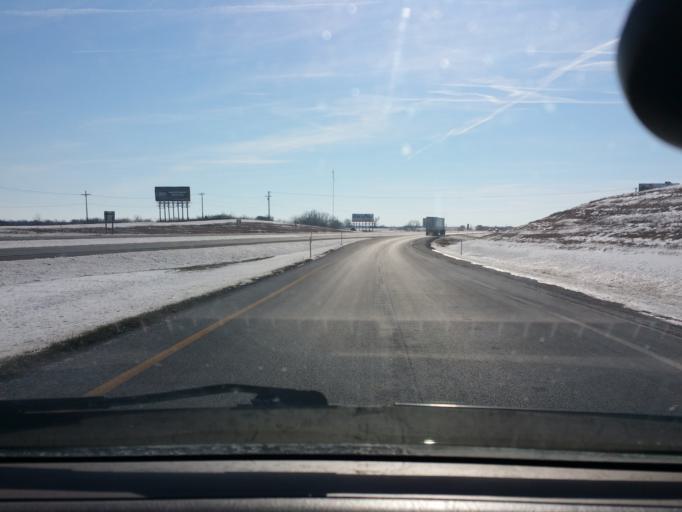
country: US
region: Missouri
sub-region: Harrison County
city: Bethany
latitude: 40.2639
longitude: -94.0134
